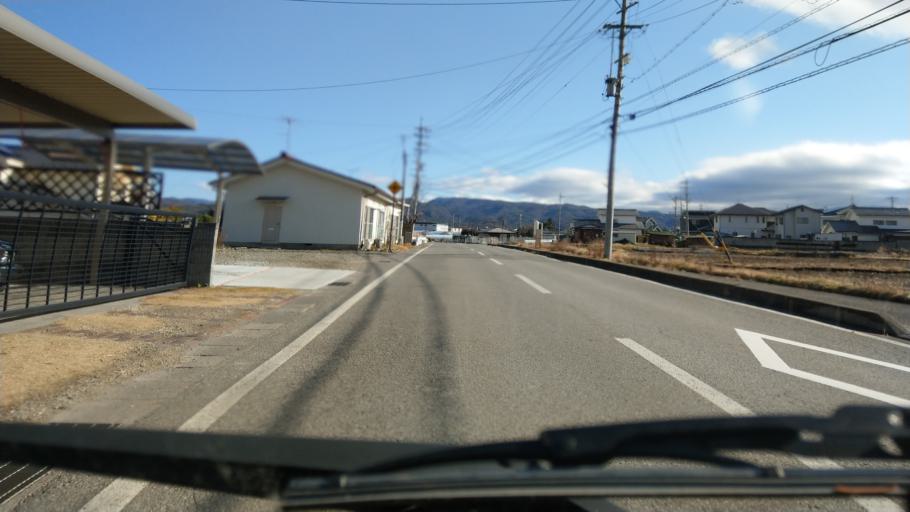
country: JP
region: Nagano
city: Saku
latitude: 36.2451
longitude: 138.4631
